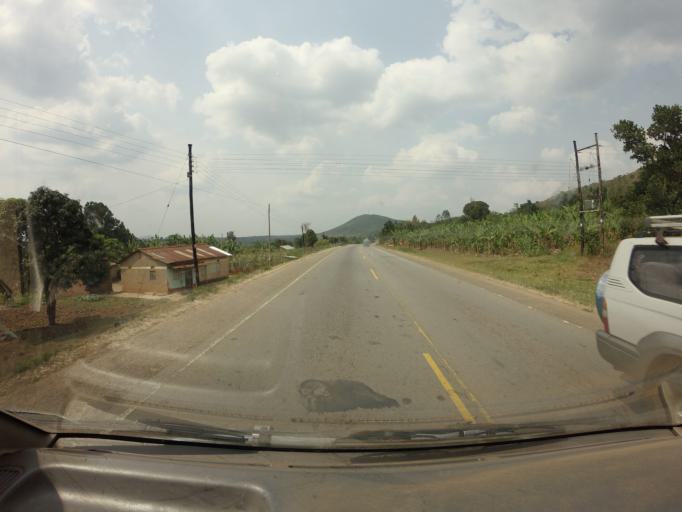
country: UG
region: Central Region
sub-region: Lyantonde District
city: Lyantonde
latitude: -0.3878
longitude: 31.1893
